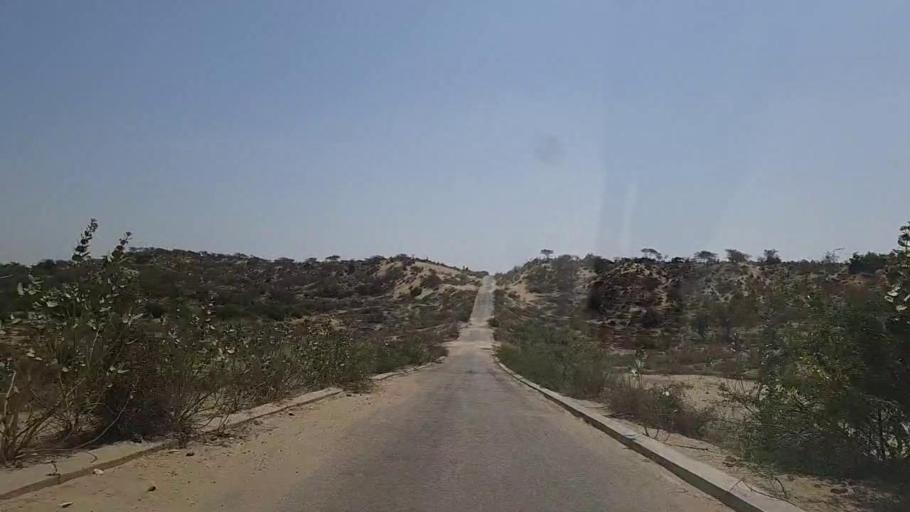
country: PK
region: Sindh
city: Diplo
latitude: 24.5083
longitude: 69.4232
